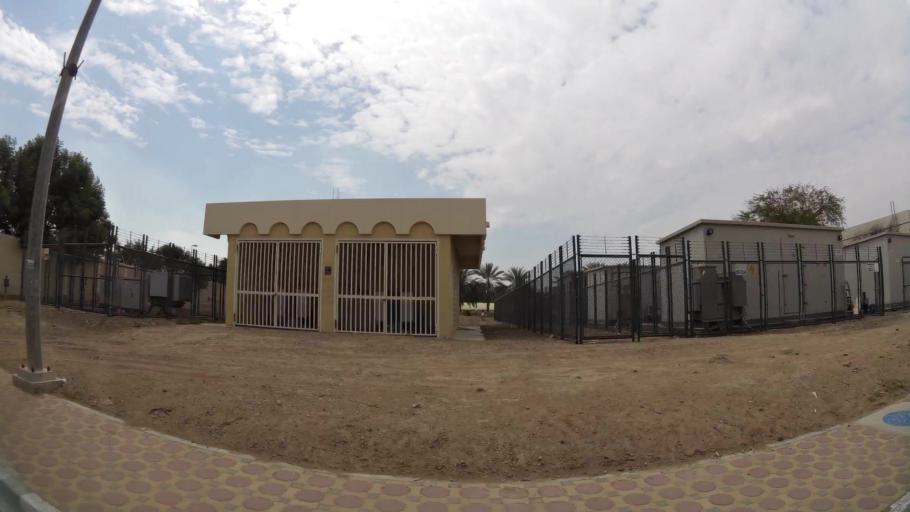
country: OM
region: Al Buraimi
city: Al Buraymi
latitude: 24.2231
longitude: 55.7885
